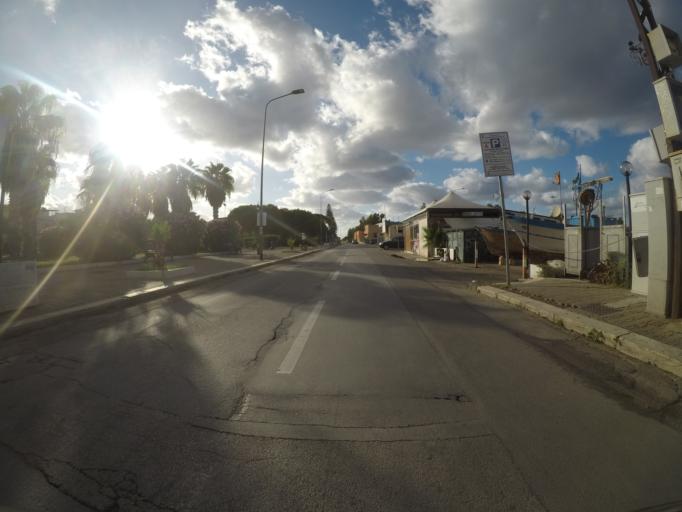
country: IT
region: Sicily
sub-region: Palermo
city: Isola delle Femmine
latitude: 38.1986
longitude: 13.2475
